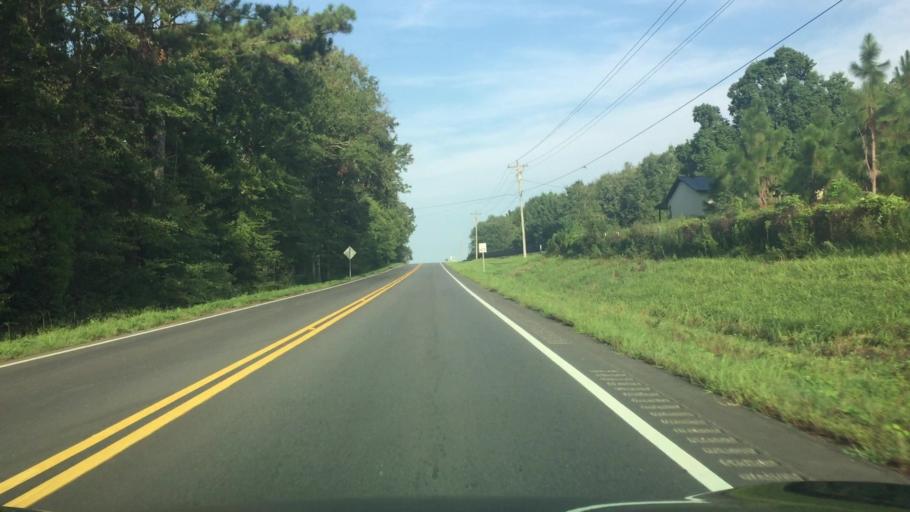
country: US
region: Alabama
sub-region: Covington County
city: Andalusia
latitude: 31.2780
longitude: -86.4993
